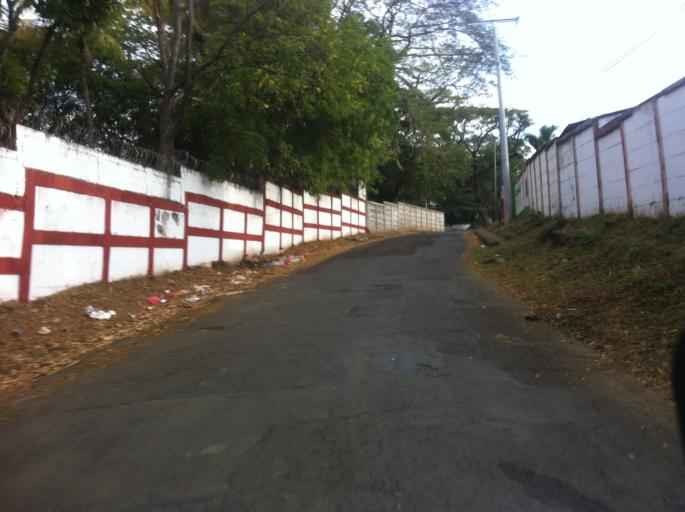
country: NI
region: Managua
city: Ciudad Sandino
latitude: 12.1054
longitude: -86.3129
